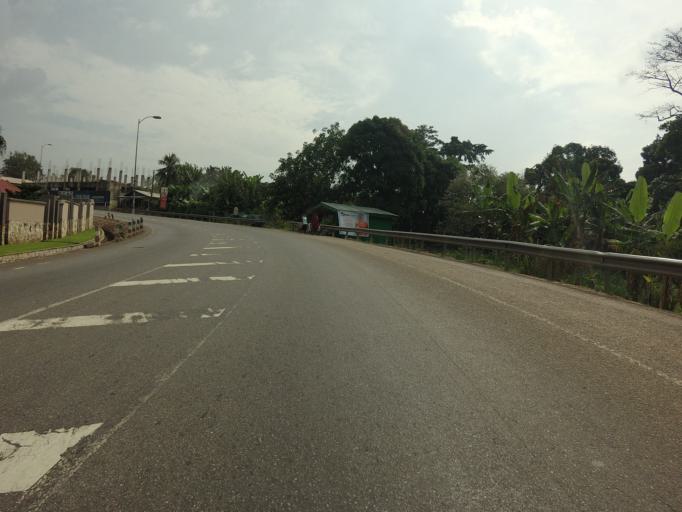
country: GH
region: Eastern
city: Aburi
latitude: 5.8149
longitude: -0.1877
